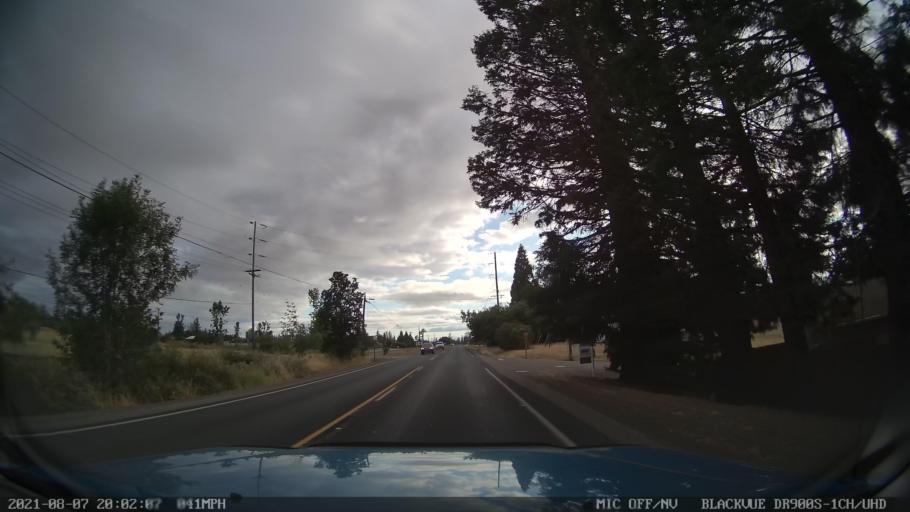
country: US
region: Oregon
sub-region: Marion County
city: Silverton
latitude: 45.0045
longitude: -122.7996
